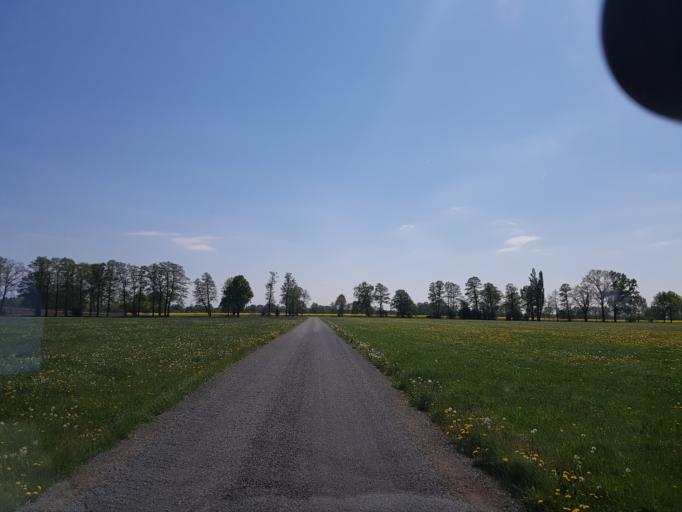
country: DE
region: Brandenburg
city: Schonewalde
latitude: 51.6698
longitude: 13.5803
